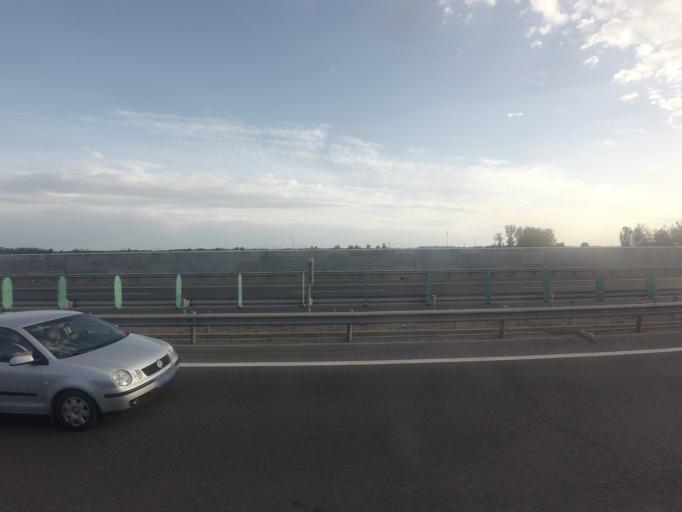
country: CN
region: Beijing
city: Yangsong
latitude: 40.2768
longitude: 116.7065
